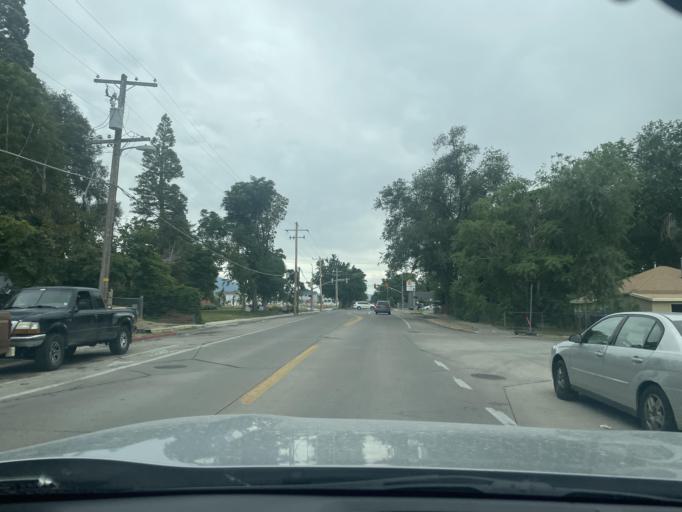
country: US
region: Utah
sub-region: Salt Lake County
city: Millcreek
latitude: 40.7010
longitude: -111.8770
